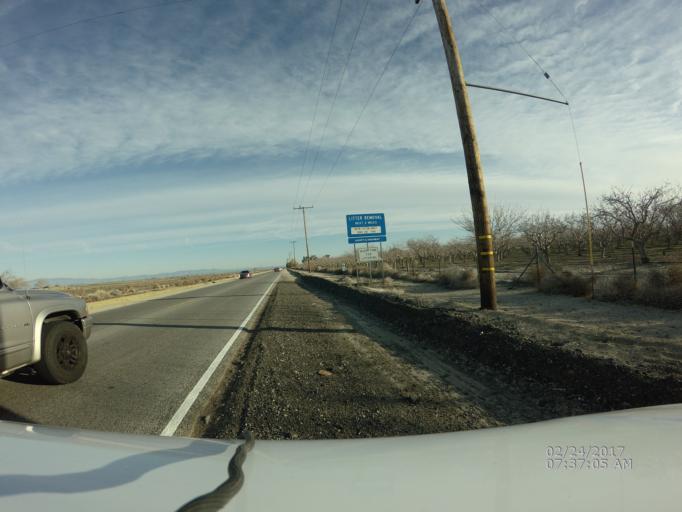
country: US
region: California
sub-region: Los Angeles County
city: Palmdale
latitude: 34.6241
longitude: -118.0409
